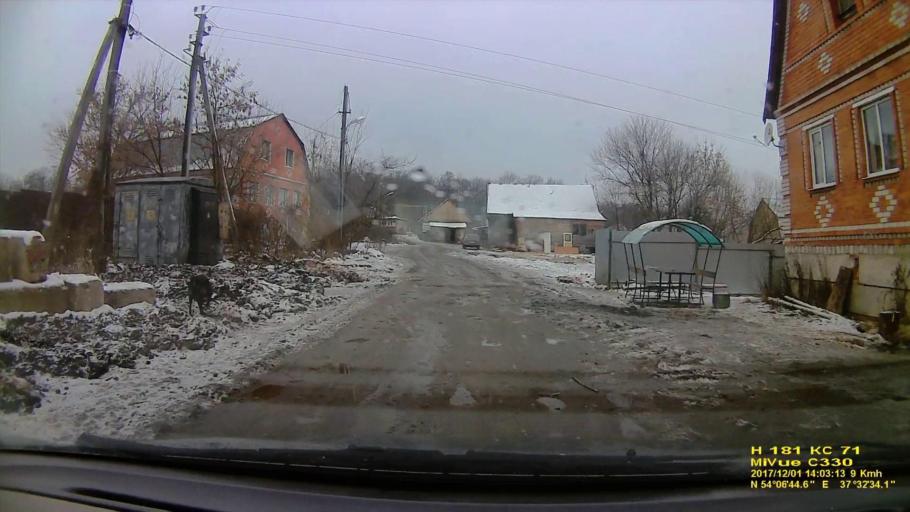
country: RU
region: Tula
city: Kosaya Gora
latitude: 54.1124
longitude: 37.5428
